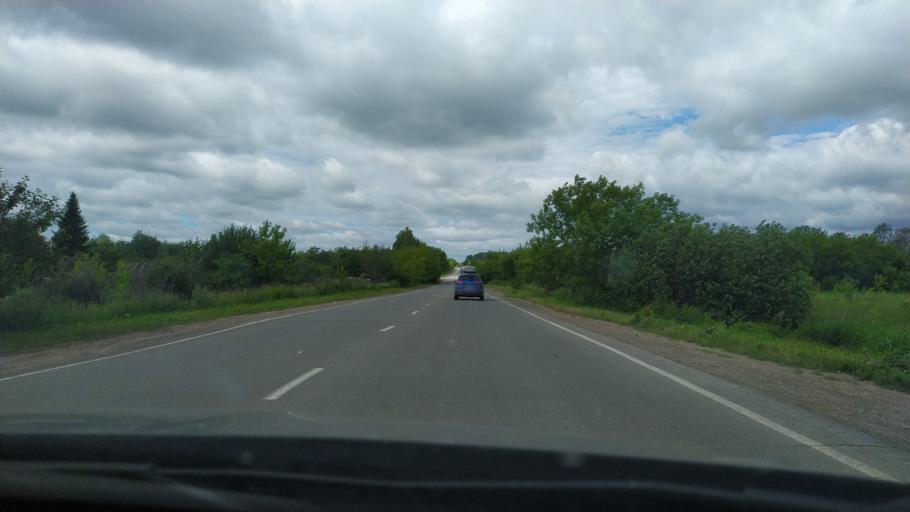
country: RU
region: Perm
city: Kondratovo
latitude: 57.9293
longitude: 56.1042
